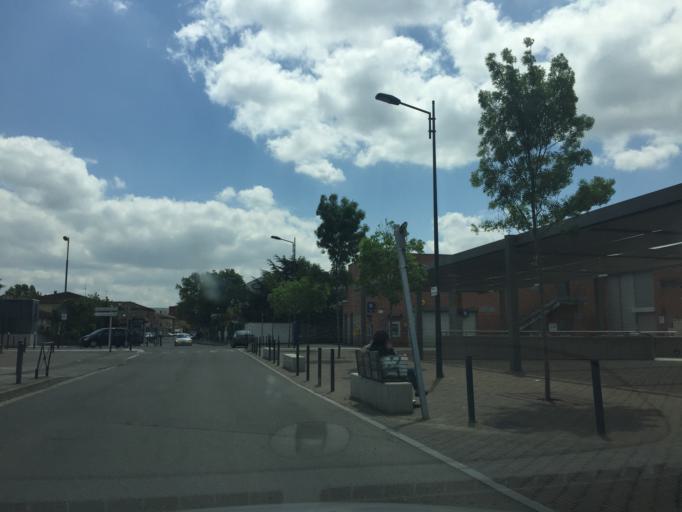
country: FR
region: Midi-Pyrenees
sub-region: Departement de la Haute-Garonne
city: Toulouse
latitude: 43.6385
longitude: 1.4442
